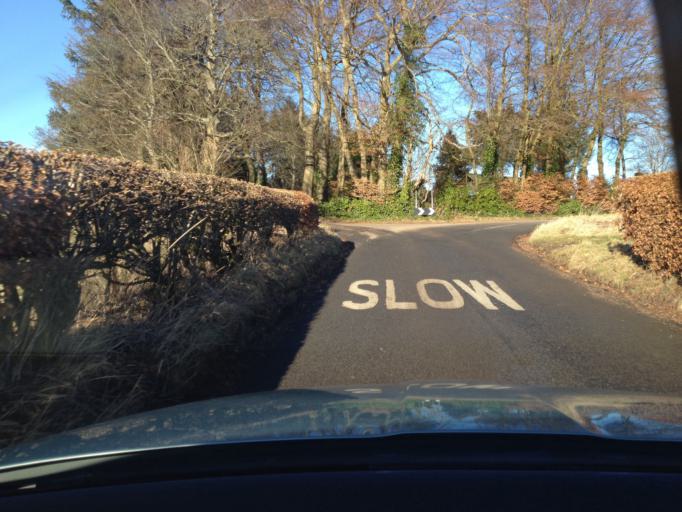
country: GB
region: Scotland
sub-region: Perth and Kinross
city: Bridge of Earn
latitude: 56.2895
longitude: -3.3962
